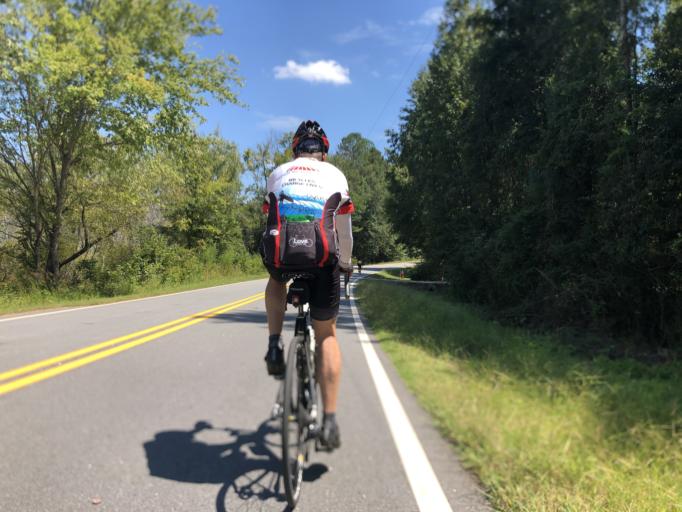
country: US
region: Georgia
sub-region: Fulton County
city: Chattahoochee Hills
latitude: 33.4872
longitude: -84.8136
